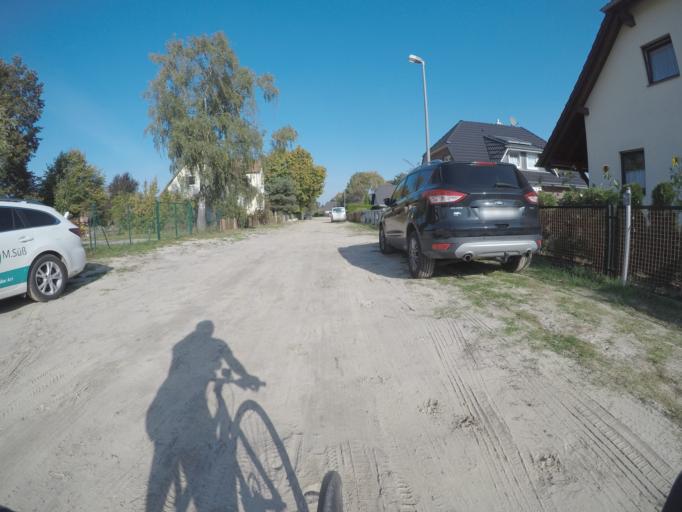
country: DE
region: Brandenburg
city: Oranienburg
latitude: 52.7353
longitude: 13.2520
